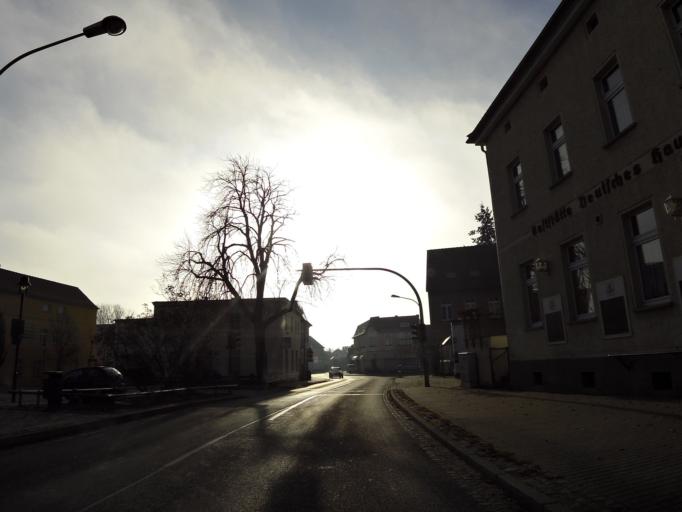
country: DE
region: Brandenburg
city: Werder
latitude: 52.3653
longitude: 12.9098
